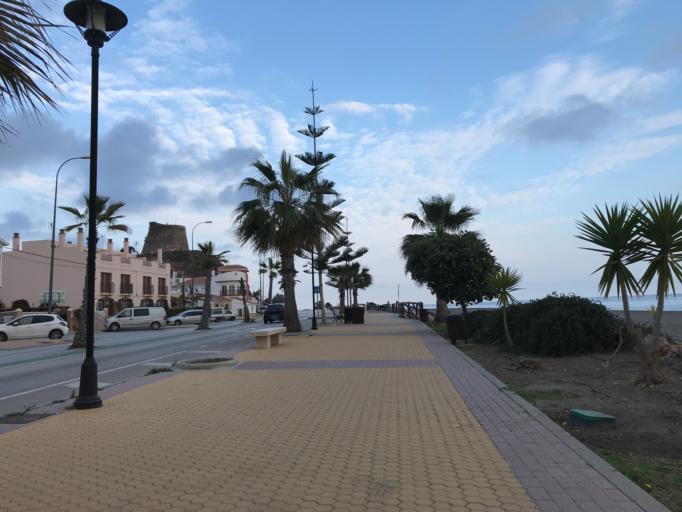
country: ES
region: Andalusia
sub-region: Provincia de Malaga
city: Iznate
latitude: 36.7157
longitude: -4.1893
